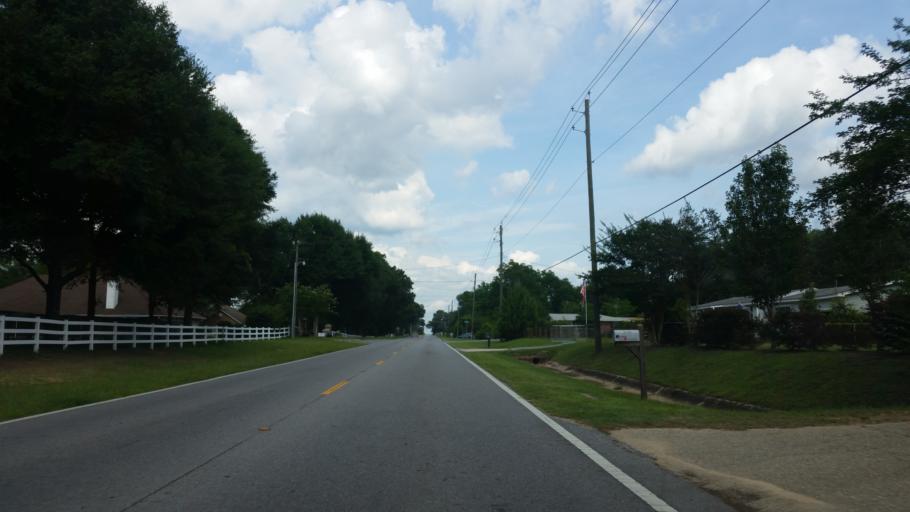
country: US
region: Florida
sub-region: Escambia County
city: Gonzalez
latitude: 30.5693
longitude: -87.2666
